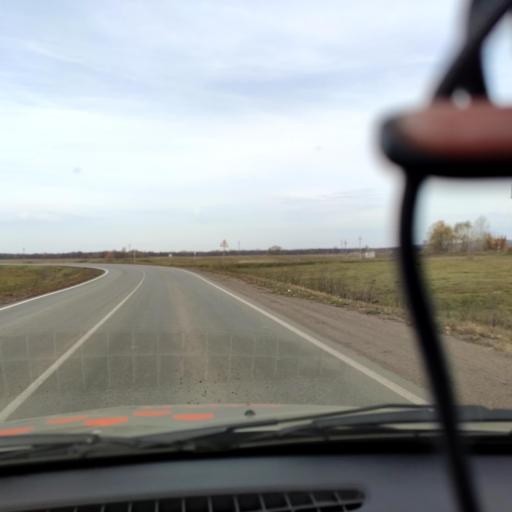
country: RU
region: Bashkortostan
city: Kabakovo
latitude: 54.5527
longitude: 56.0238
